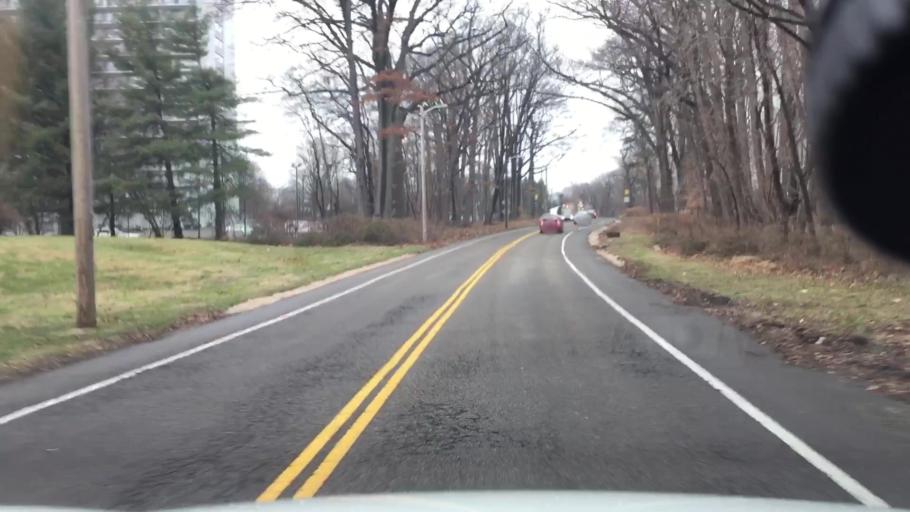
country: US
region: Pennsylvania
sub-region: Montgomery County
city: Wyndmoor
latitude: 40.0717
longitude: -75.1909
